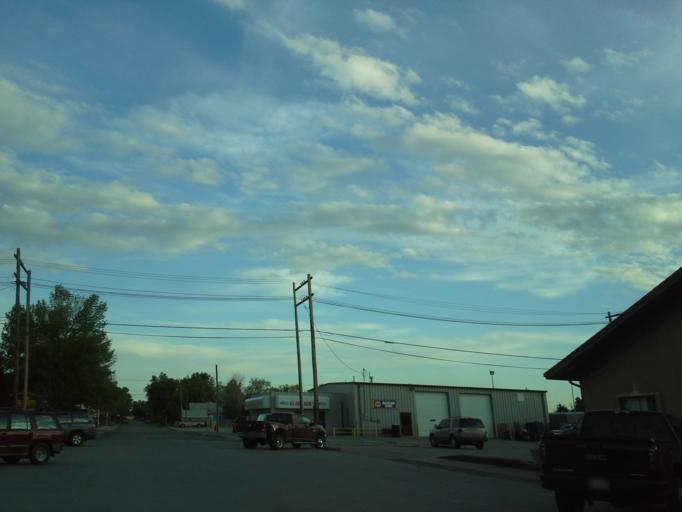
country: US
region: Wyoming
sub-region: Washakie County
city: Worland
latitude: 44.0167
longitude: -107.9613
